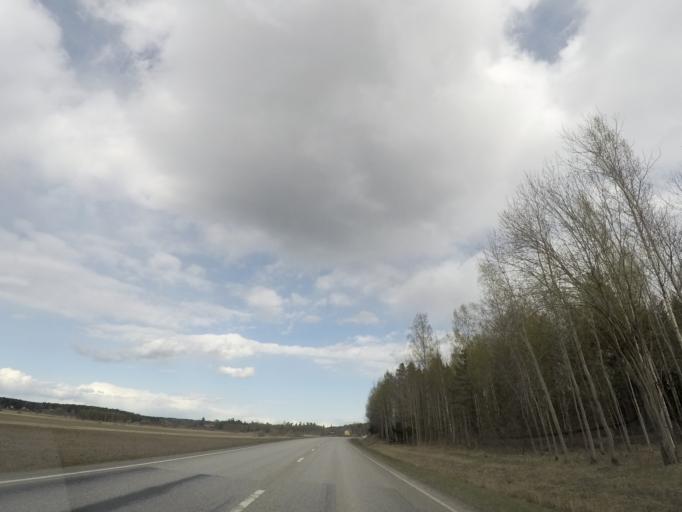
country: SE
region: Soedermanland
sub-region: Eskilstuna Kommun
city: Hallbybrunn
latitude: 59.3198
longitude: 16.3657
